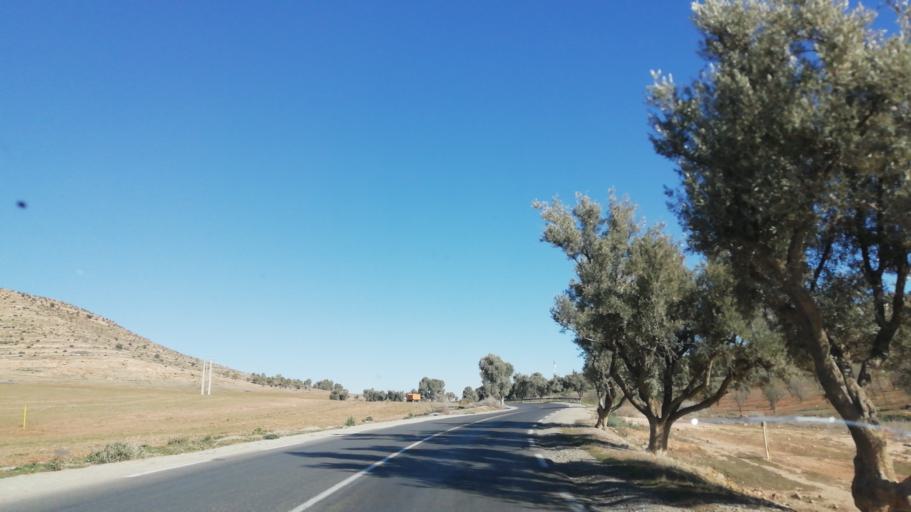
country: DZ
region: Mascara
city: Mascara
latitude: 35.2411
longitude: 0.1183
